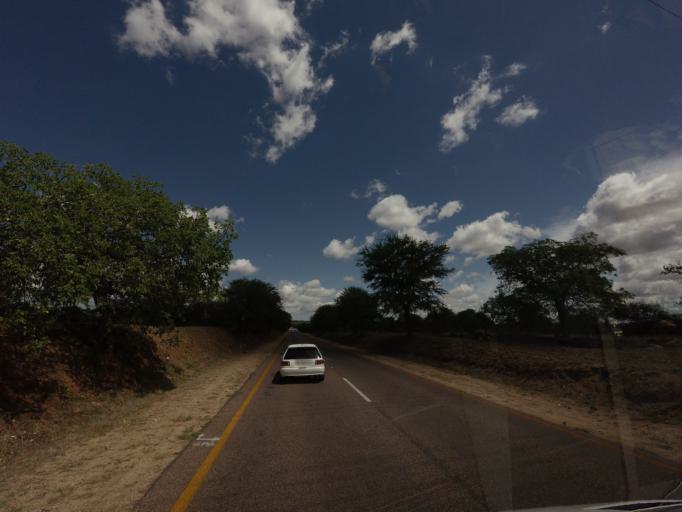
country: ZA
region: Limpopo
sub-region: Mopani District Municipality
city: Hoedspruit
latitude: -24.3570
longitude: 30.9617
